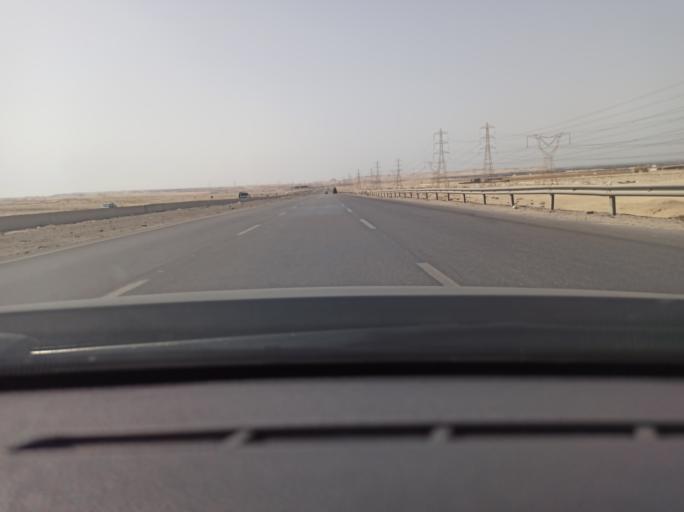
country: EG
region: Muhafazat al Qahirah
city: Halwan
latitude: 29.7428
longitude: 31.4100
